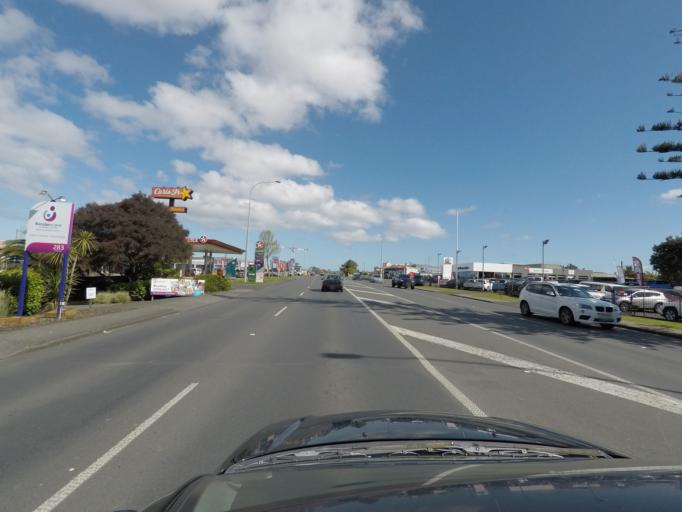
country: NZ
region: Auckland
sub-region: Auckland
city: Rosebank
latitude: -36.8540
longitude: 174.6301
